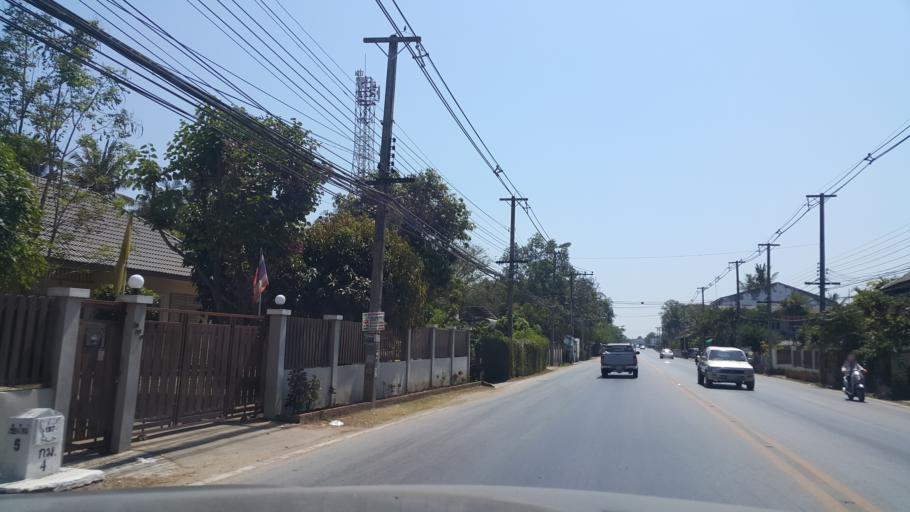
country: TH
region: Chiang Mai
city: San Sai
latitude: 18.8433
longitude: 99.0435
